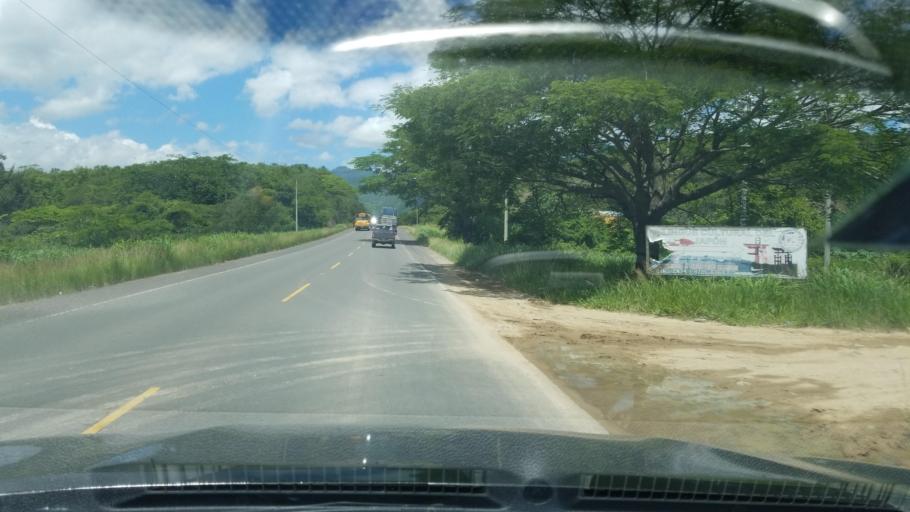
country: HN
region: Francisco Morazan
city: Cofradia
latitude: 14.2747
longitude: -87.2438
